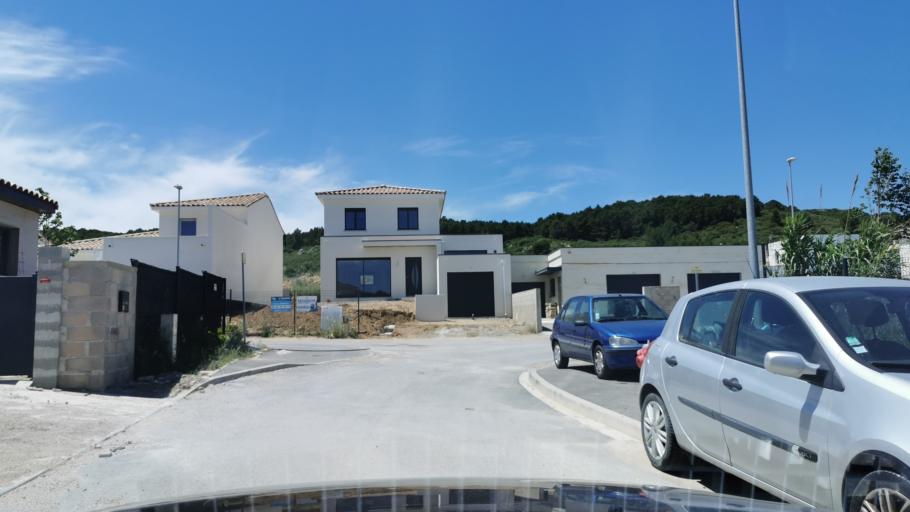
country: FR
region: Languedoc-Roussillon
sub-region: Departement de l'Aude
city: Moussan
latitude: 43.1945
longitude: 2.9625
